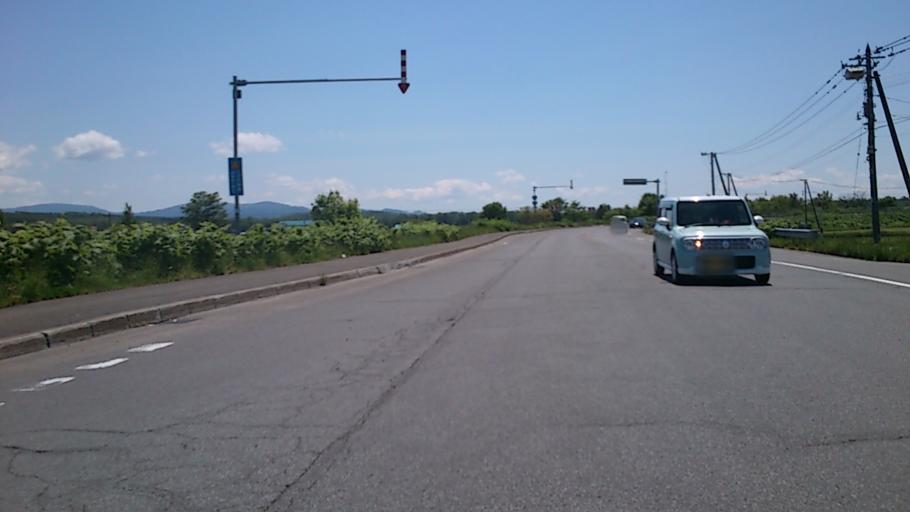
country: JP
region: Hokkaido
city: Nayoro
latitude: 44.3166
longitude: 142.4570
